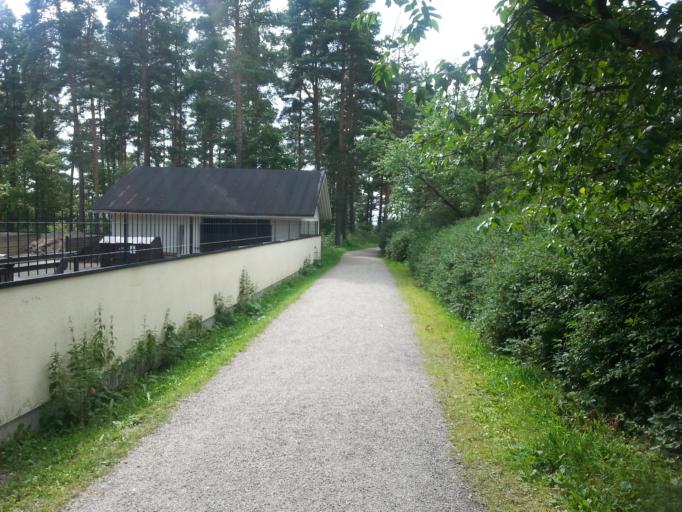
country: FI
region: Paijanne Tavastia
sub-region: Lahti
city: Lahti
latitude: 60.9790
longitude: 25.6502
